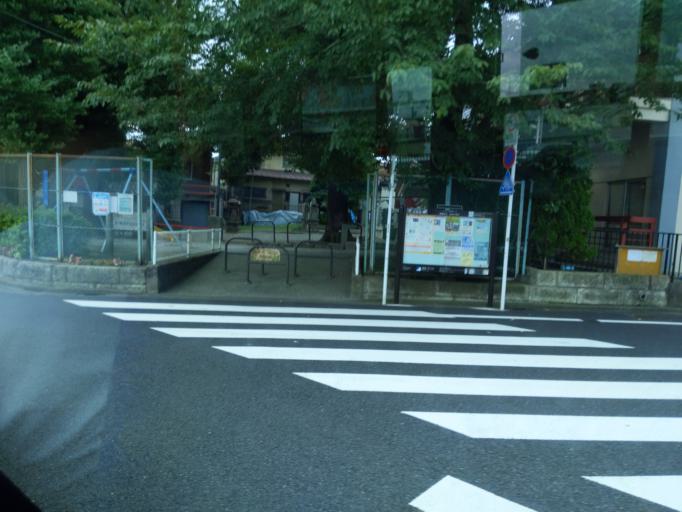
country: JP
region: Kanagawa
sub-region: Kawasaki-shi
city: Kawasaki
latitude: 35.5860
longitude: 139.6935
